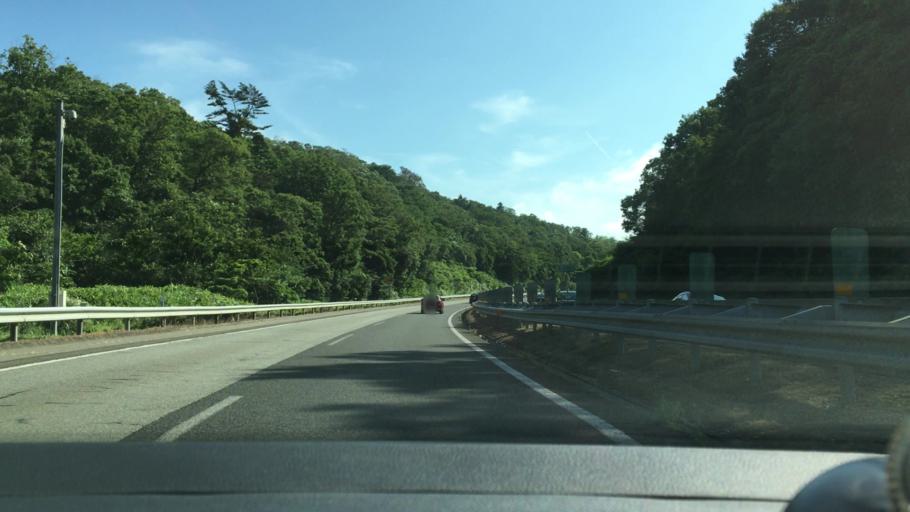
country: JP
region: Ishikawa
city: Komatsu
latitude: 36.3223
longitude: 136.3046
